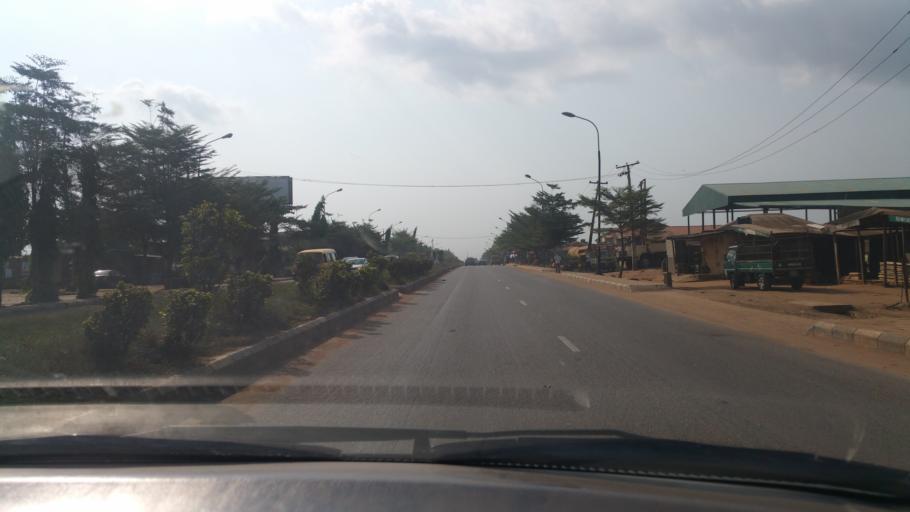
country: NG
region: Lagos
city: Ikotun
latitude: 6.5770
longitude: 3.2713
